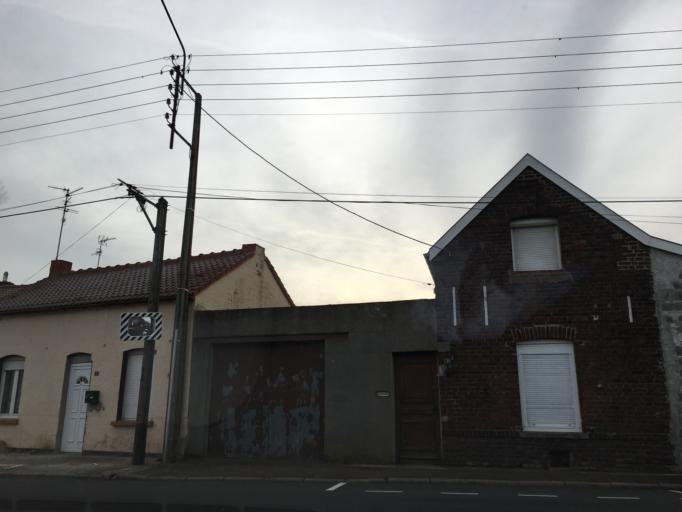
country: FR
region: Nord-Pas-de-Calais
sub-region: Departement du Pas-de-Calais
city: Courrieres
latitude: 50.4511
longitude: 2.9425
